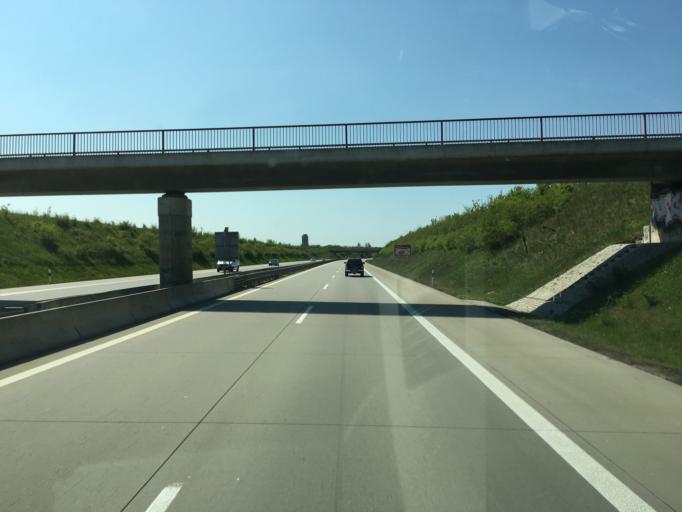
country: DE
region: Saxony
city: Grossposna
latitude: 51.2730
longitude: 12.4894
